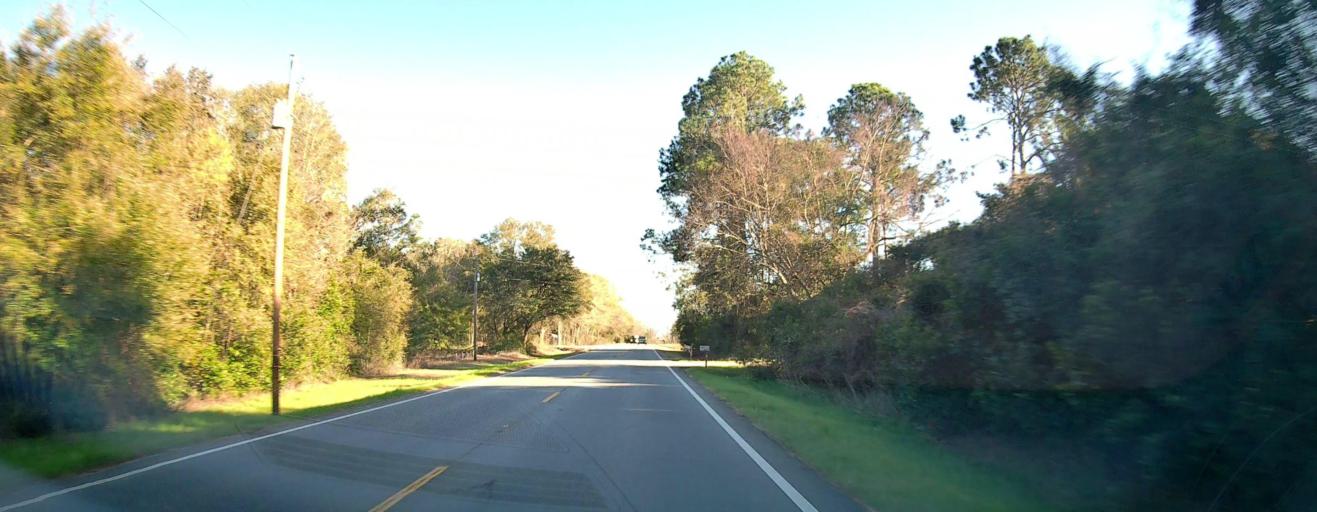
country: US
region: Georgia
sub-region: Dougherty County
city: Albany
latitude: 31.6394
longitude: -84.1667
